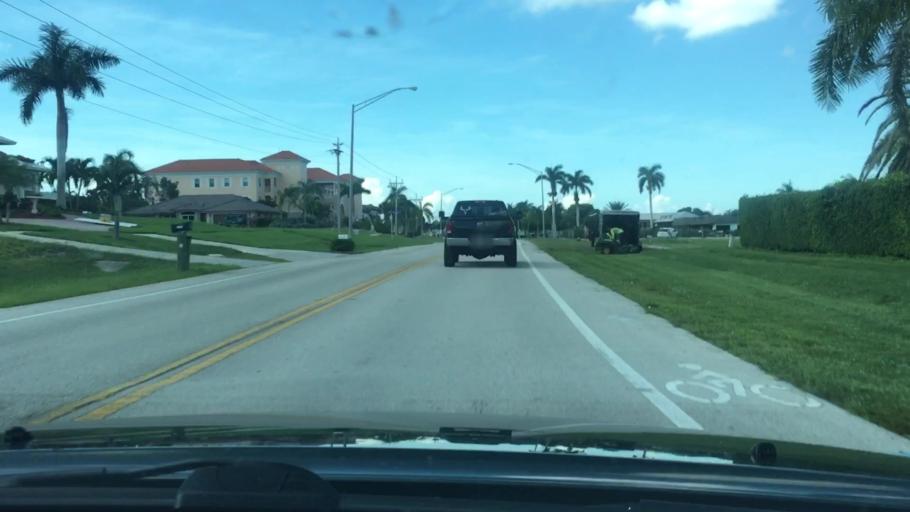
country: US
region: Florida
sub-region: Collier County
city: Marco
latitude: 25.9362
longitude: -81.6947
